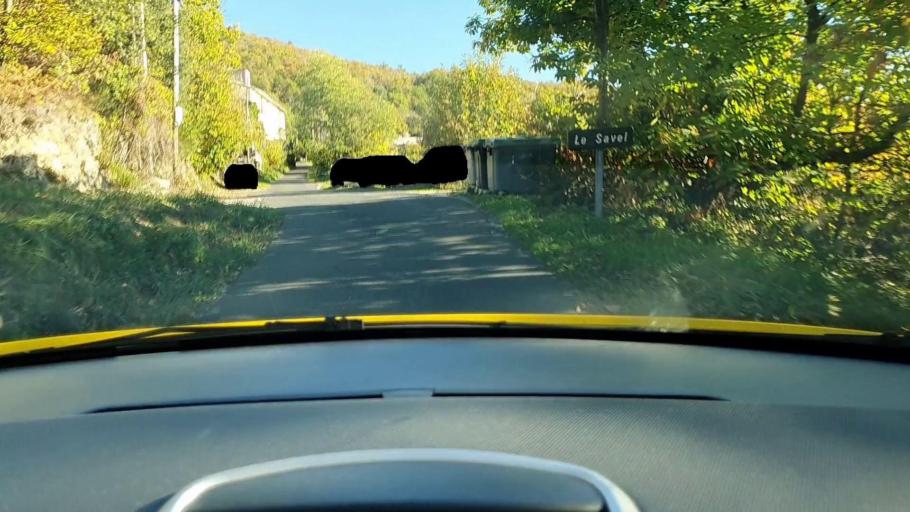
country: FR
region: Languedoc-Roussillon
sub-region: Departement du Gard
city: Sumene
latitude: 44.0189
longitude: 3.7733
